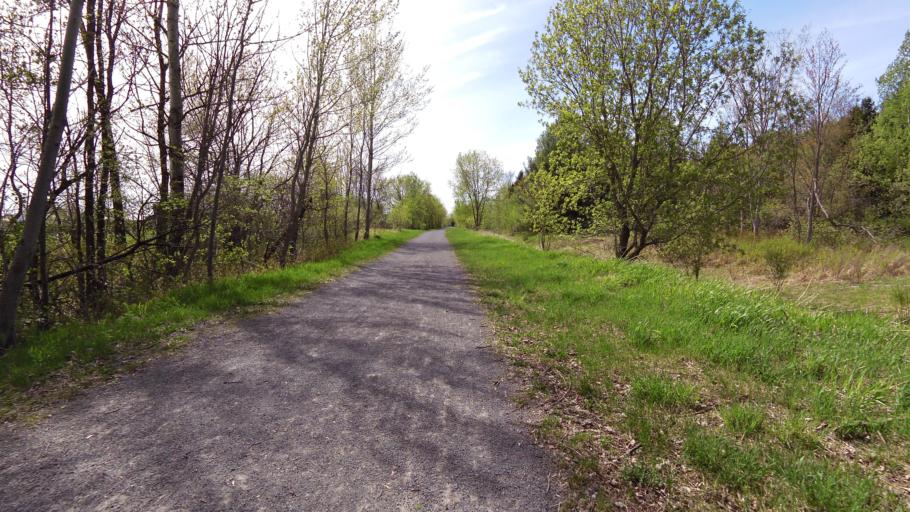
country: CA
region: Ontario
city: Clarence-Rockland
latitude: 45.4142
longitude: -75.4199
